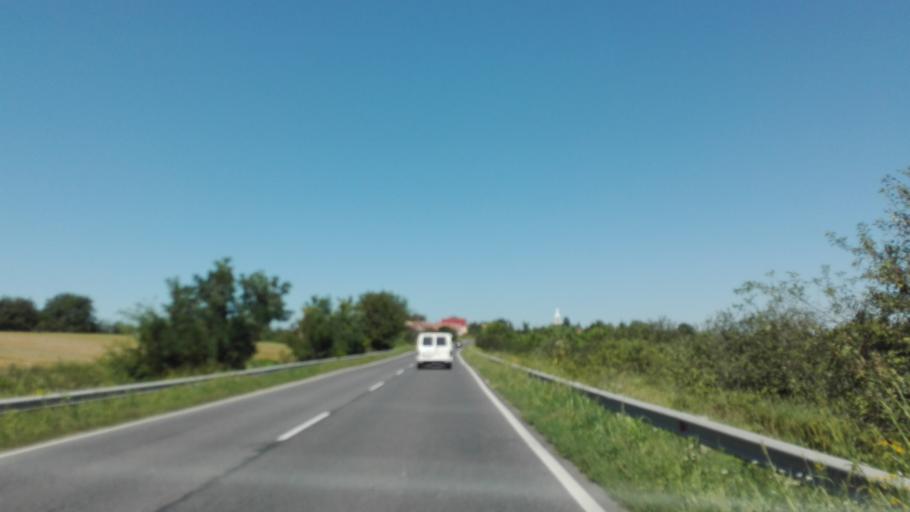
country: HU
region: Tolna
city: Simontornya
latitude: 46.7694
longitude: 18.5186
